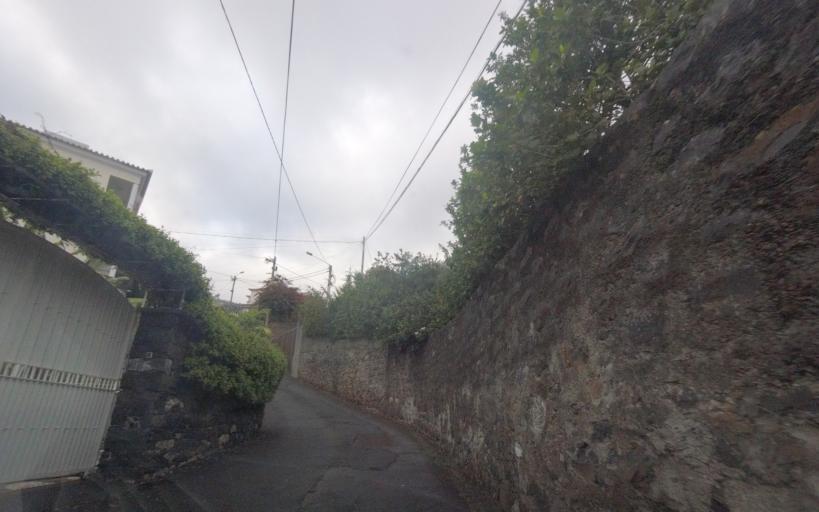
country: PT
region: Madeira
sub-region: Funchal
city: Nossa Senhora do Monte
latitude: 32.6569
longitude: -16.8937
